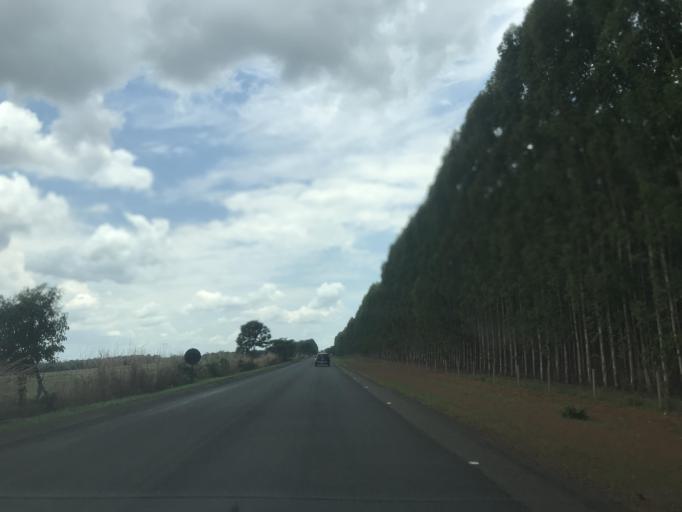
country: BR
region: Goias
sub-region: Vianopolis
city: Vianopolis
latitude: -16.9287
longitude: -48.5579
